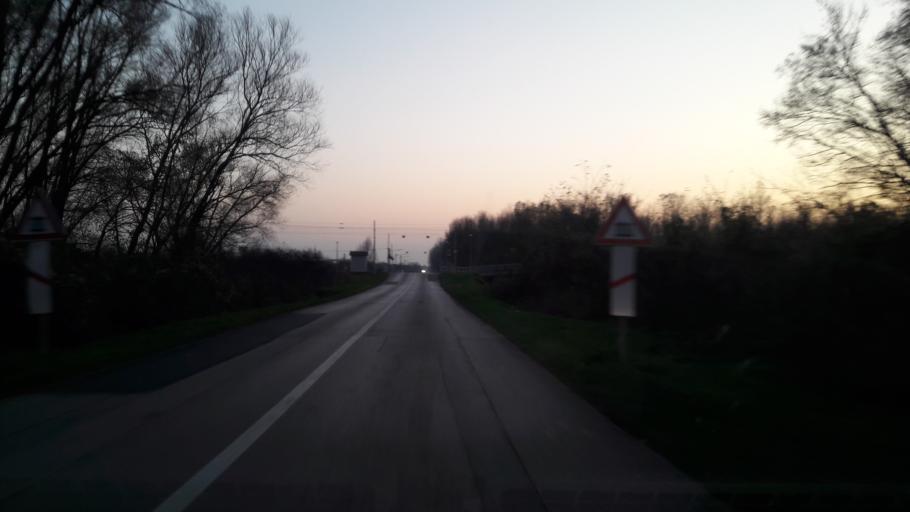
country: HR
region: Vukovarsko-Srijemska
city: Nijemci
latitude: 45.1947
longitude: 19.0204
